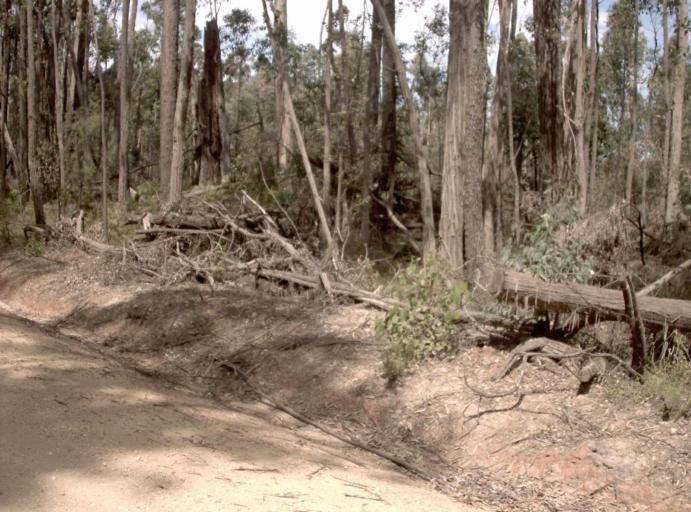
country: AU
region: Victoria
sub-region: East Gippsland
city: Lakes Entrance
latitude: -37.6556
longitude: 148.6503
